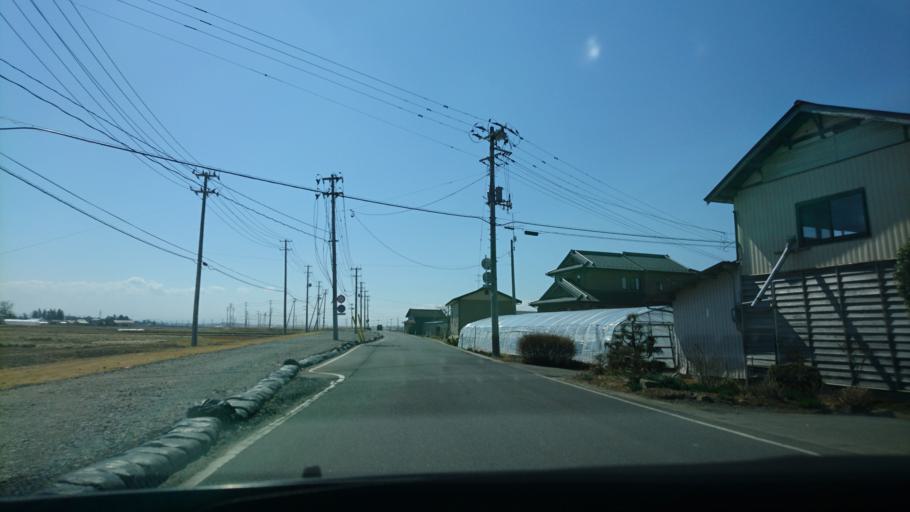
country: JP
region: Iwate
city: Ichinoseki
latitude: 38.7583
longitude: 141.1323
